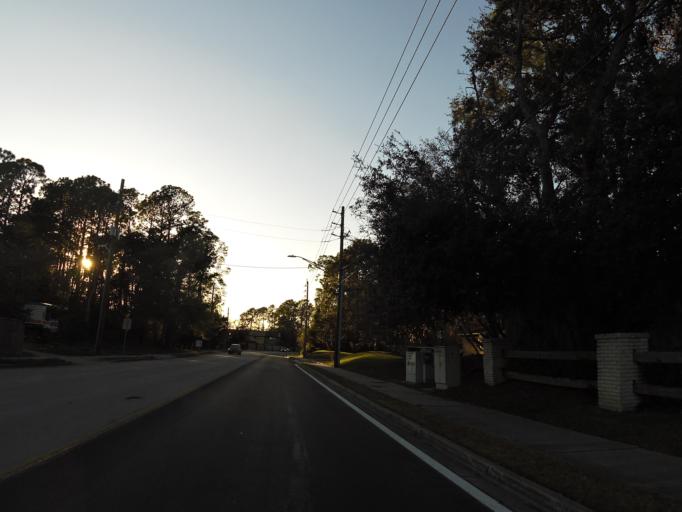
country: US
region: Florida
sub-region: Saint Johns County
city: Fruit Cove
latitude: 30.1722
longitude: -81.5970
